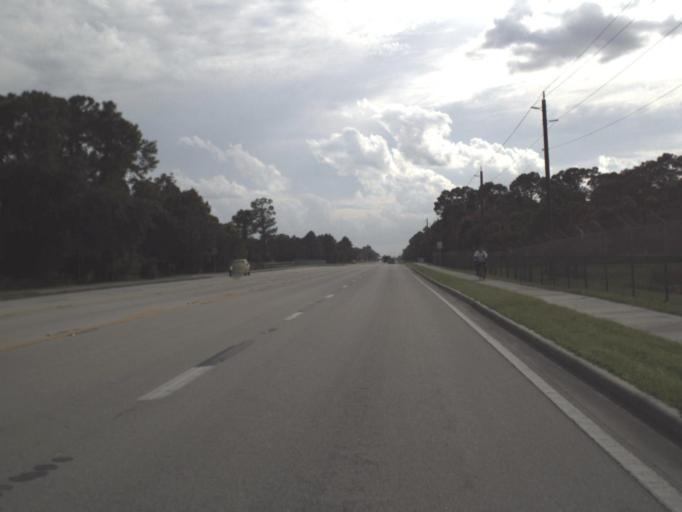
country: US
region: Florida
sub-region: Hendry County
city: LaBelle
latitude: 26.7577
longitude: -81.4533
